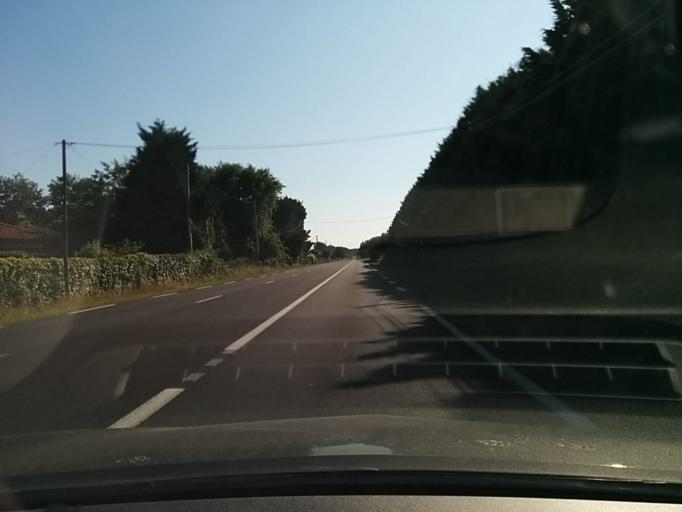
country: FR
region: Aquitaine
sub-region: Departement des Landes
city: Benesse-Maremne
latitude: 43.6232
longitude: -1.3819
